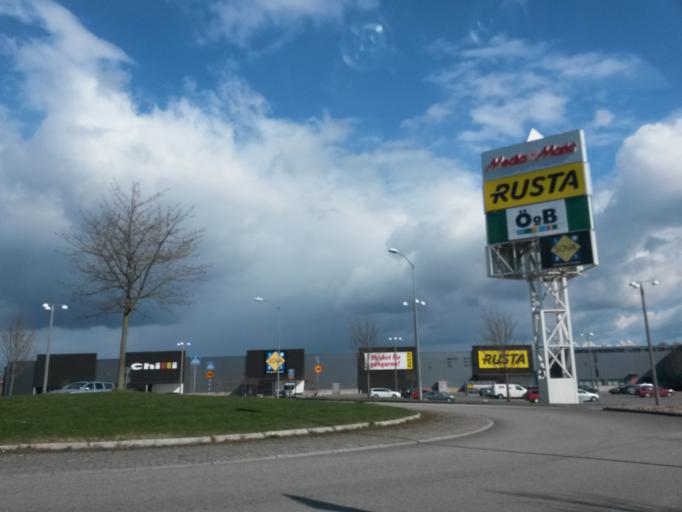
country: SE
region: Vaestra Goetaland
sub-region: Skovde Kommun
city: Skoevde
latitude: 58.4119
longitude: 13.8770
